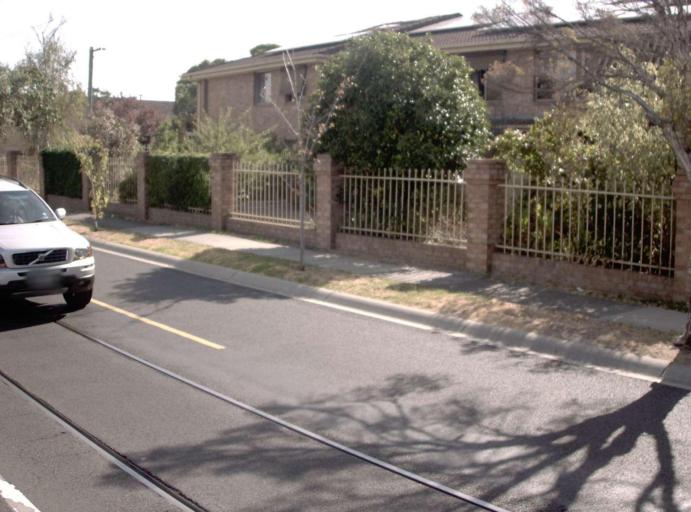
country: AU
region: Victoria
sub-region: Bayside
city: Brighton East
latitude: -37.9079
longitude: 145.0180
